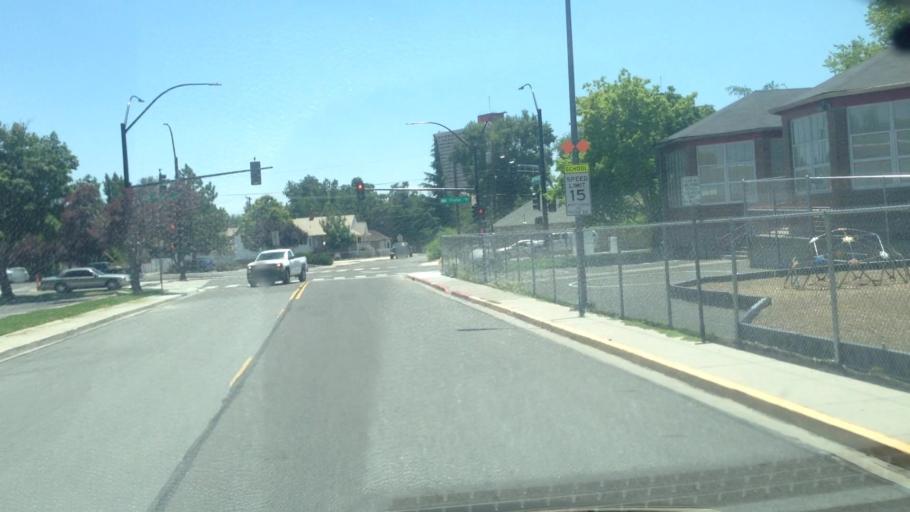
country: US
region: Nevada
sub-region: Washoe County
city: Sparks
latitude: 39.5399
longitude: -119.7583
